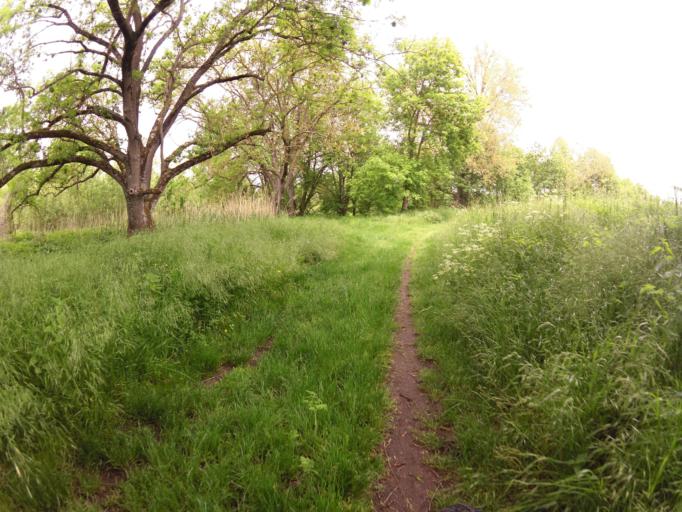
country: DE
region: Bavaria
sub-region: Regierungsbezirk Unterfranken
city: Sommerach
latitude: 49.8302
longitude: 10.1917
